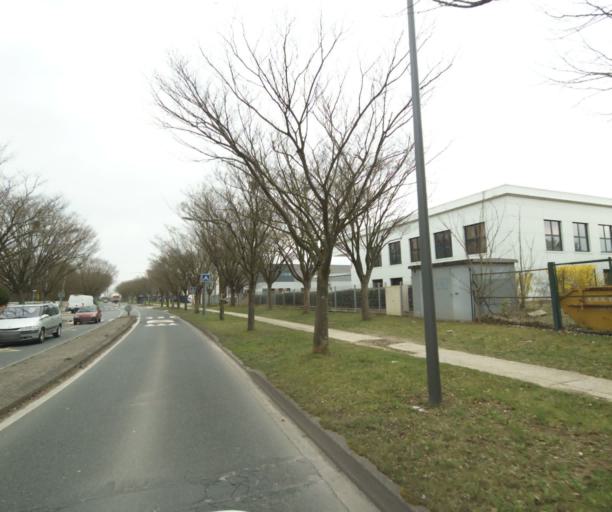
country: FR
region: Ile-de-France
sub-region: Departement du Val-d'Oise
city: Osny
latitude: 49.0541
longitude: 2.0432
